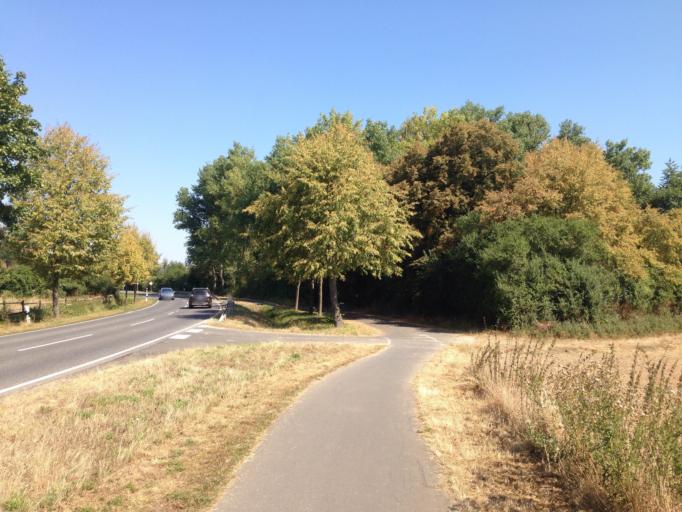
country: DE
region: Hesse
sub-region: Regierungsbezirk Giessen
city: Giessen
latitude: 50.6109
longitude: 8.6788
